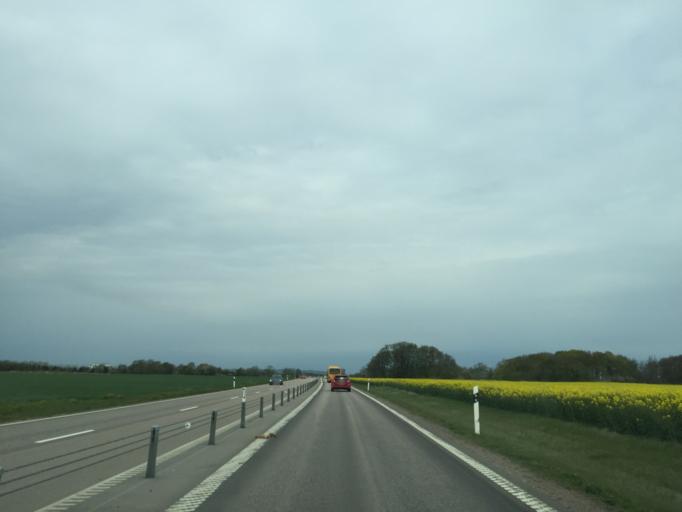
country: SE
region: Skane
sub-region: Hoganas Kommun
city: Hoganas
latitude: 56.1492
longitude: 12.5957
